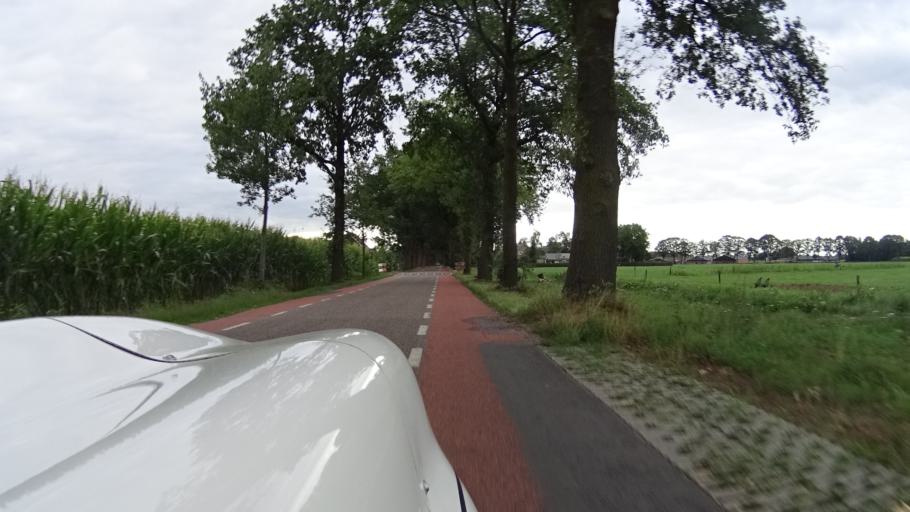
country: NL
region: North Brabant
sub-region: Gemeente Bernheze
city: Loosbroek
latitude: 51.6726
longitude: 5.5303
